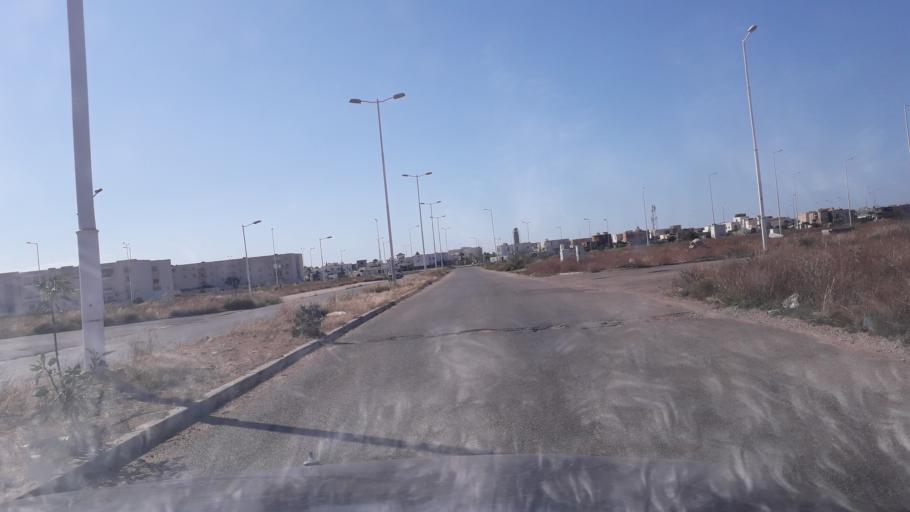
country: TN
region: Safaqis
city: Al Qarmadah
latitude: 34.8336
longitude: 10.7543
